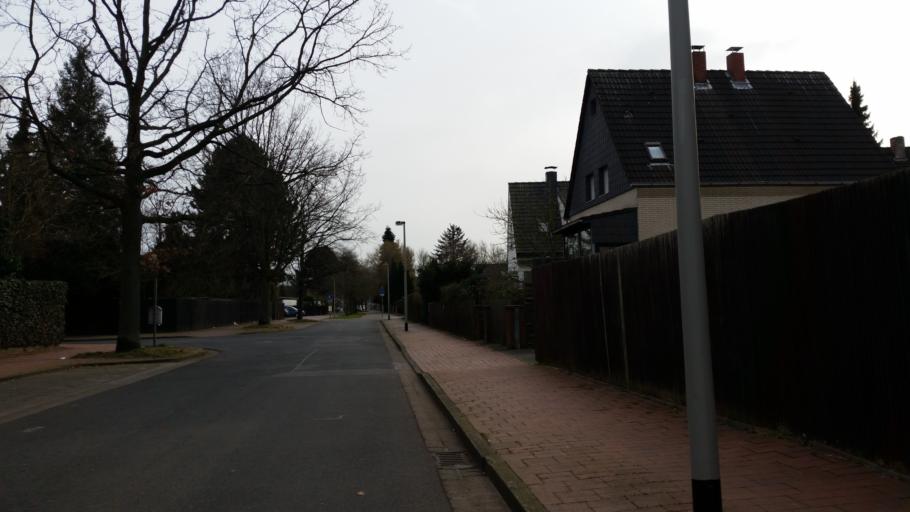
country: DE
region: Lower Saxony
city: Langenhagen
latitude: 52.4131
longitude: 9.7728
